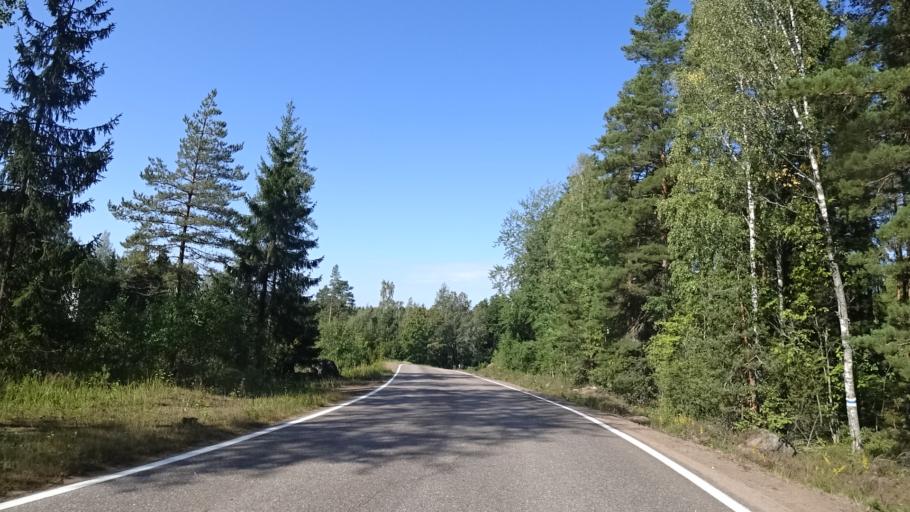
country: FI
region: Kymenlaakso
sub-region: Kotka-Hamina
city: Hamina
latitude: 60.5371
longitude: 27.2771
